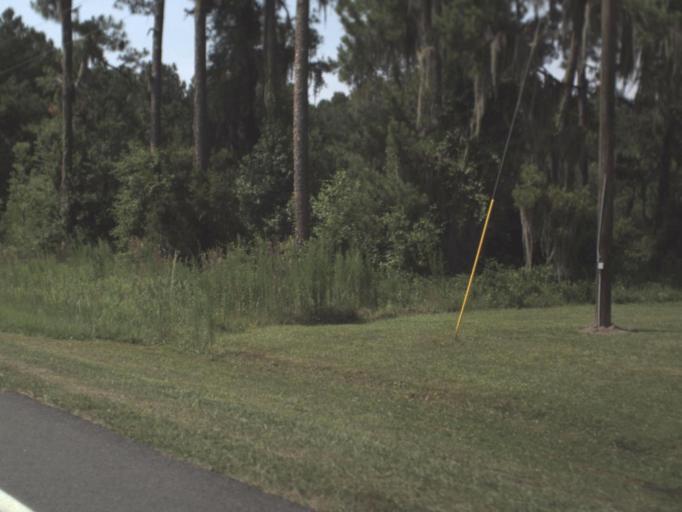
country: US
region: Florida
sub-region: Hamilton County
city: Jasper
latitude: 30.5439
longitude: -82.9759
